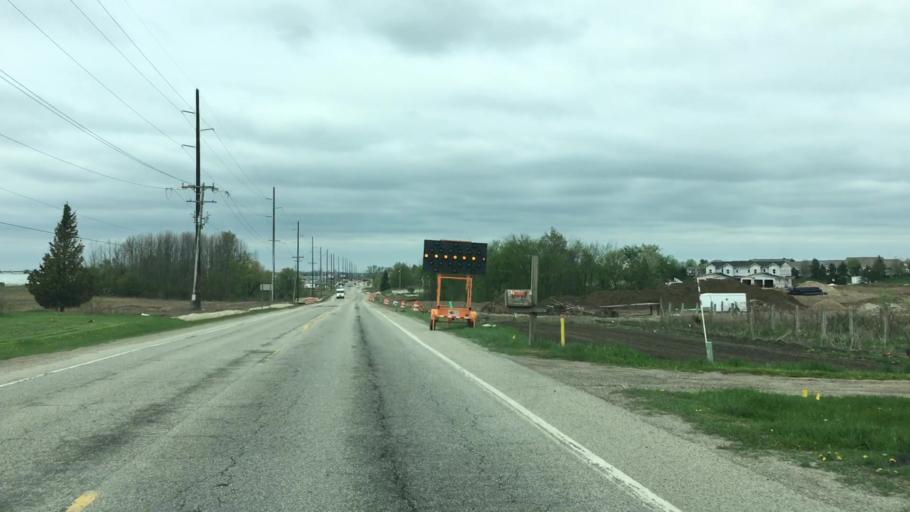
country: US
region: Michigan
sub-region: Ottawa County
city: Hudsonville
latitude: 42.8336
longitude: -85.8618
